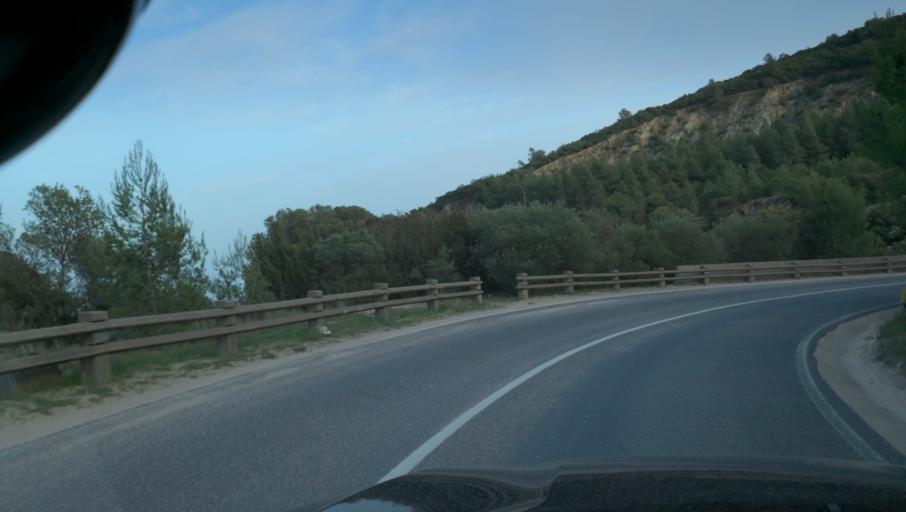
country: PT
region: Setubal
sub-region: Setubal
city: Setubal
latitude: 38.4947
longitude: -8.9410
